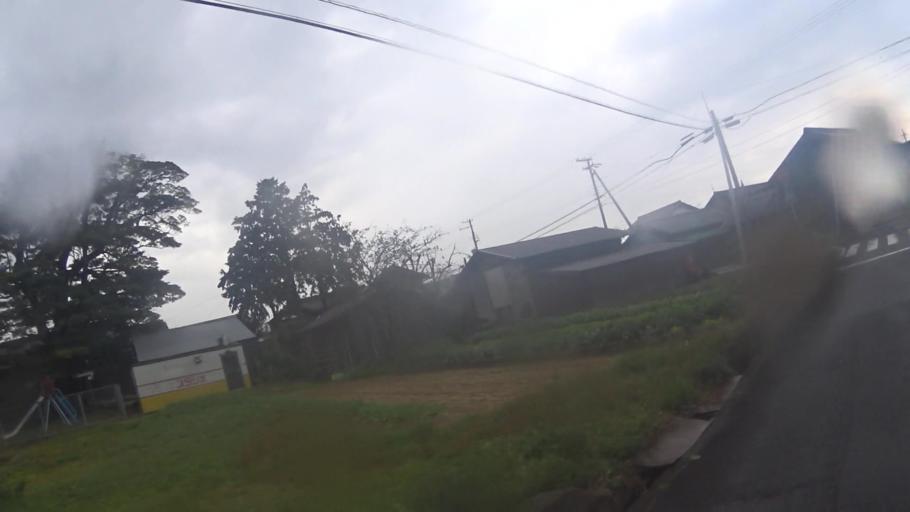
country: JP
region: Kyoto
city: Miyazu
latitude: 35.5370
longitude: 135.2408
